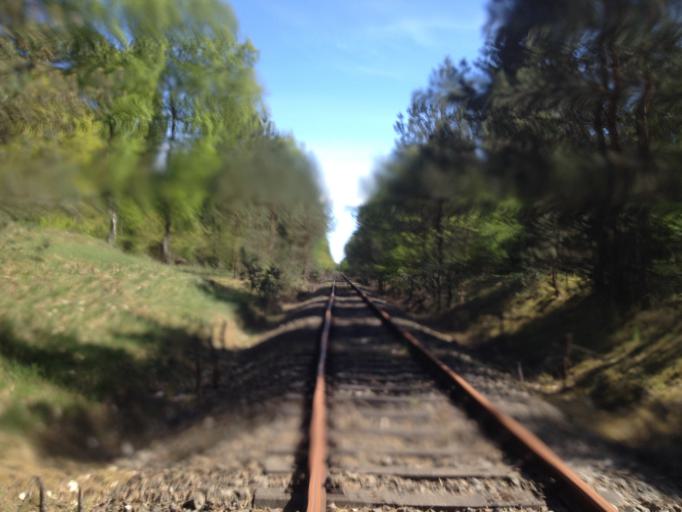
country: DE
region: Brandenburg
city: Lychen
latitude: 53.1673
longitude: 13.3693
